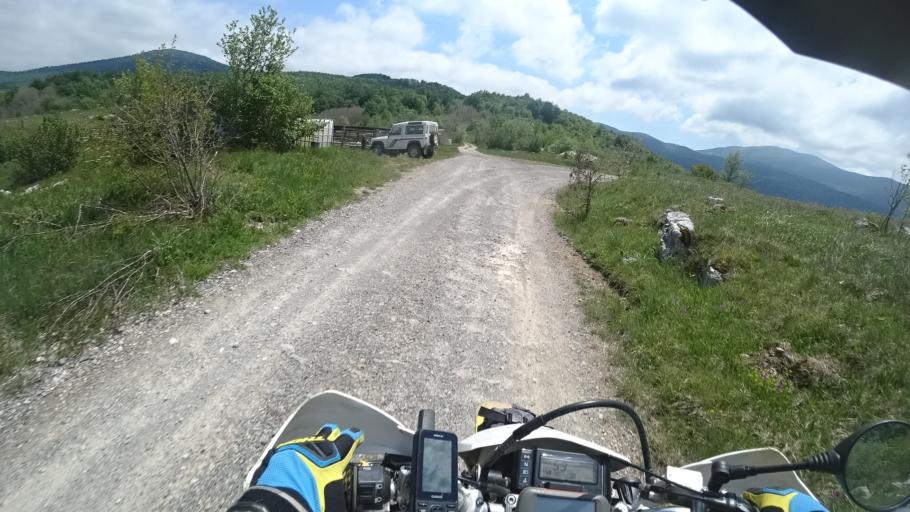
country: HR
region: Zadarska
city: Gracac
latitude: 44.5080
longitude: 15.8867
